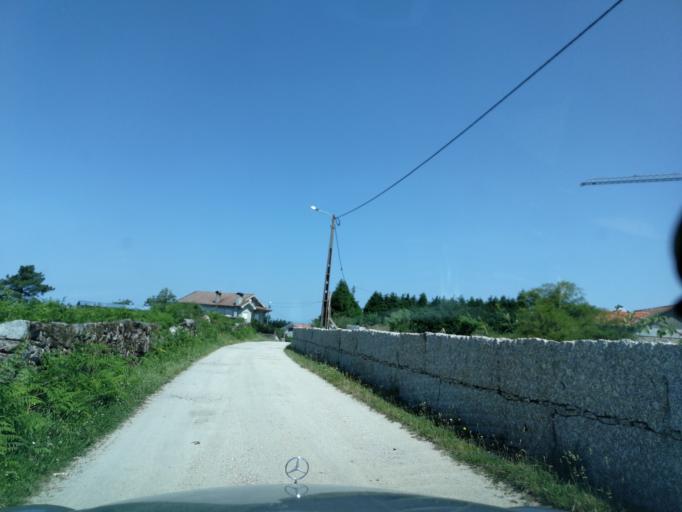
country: PT
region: Braga
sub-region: Povoa de Lanhoso
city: Povoa de Lanhoso
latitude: 41.5814
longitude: -8.3322
